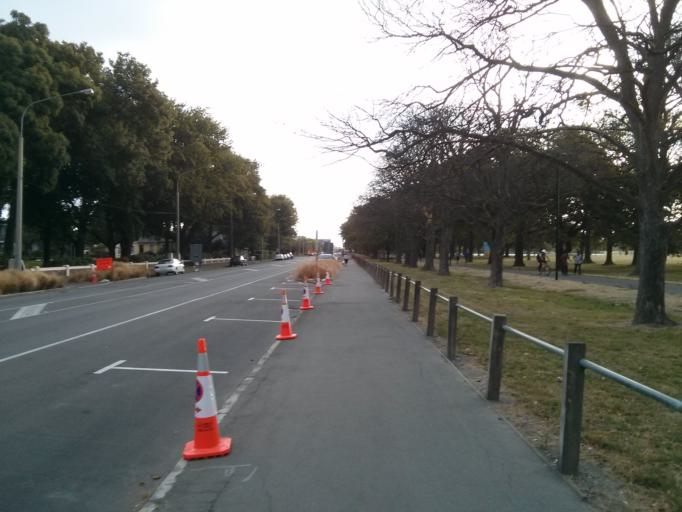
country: NZ
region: Canterbury
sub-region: Christchurch City
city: Christchurch
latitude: -43.5365
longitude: 172.6235
